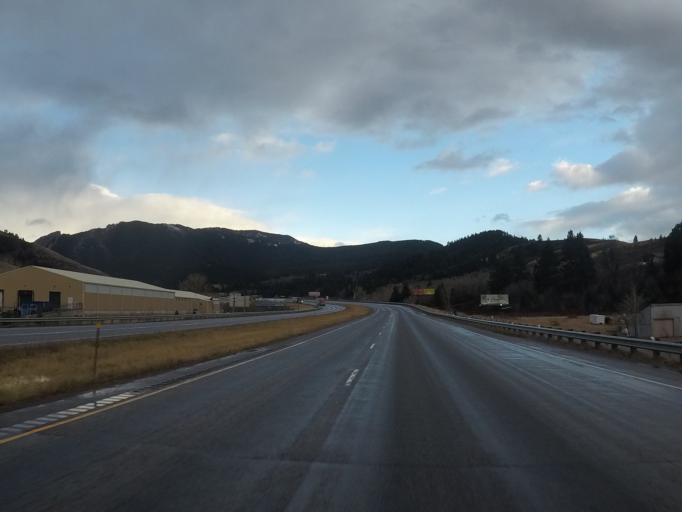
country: US
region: Montana
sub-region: Gallatin County
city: Bozeman
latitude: 45.6515
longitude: -110.9430
